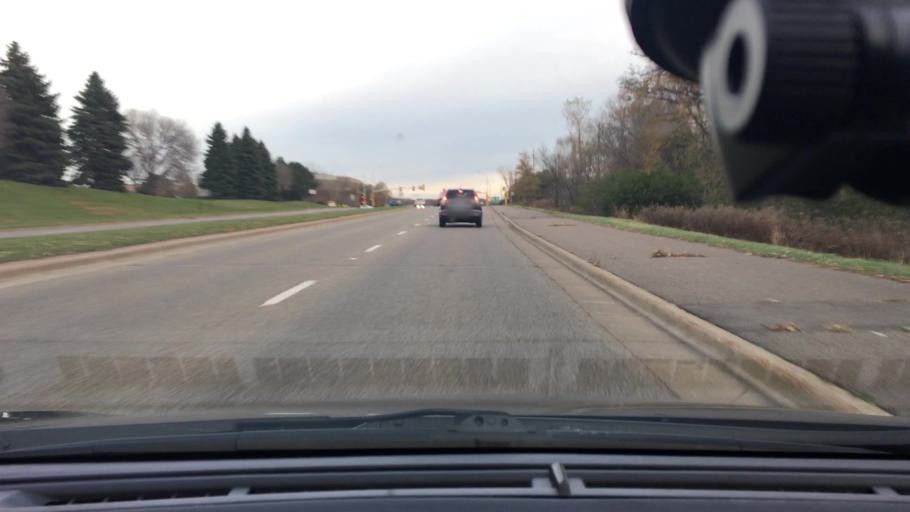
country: US
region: Minnesota
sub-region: Hennepin County
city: New Hope
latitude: 45.0584
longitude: -93.4116
